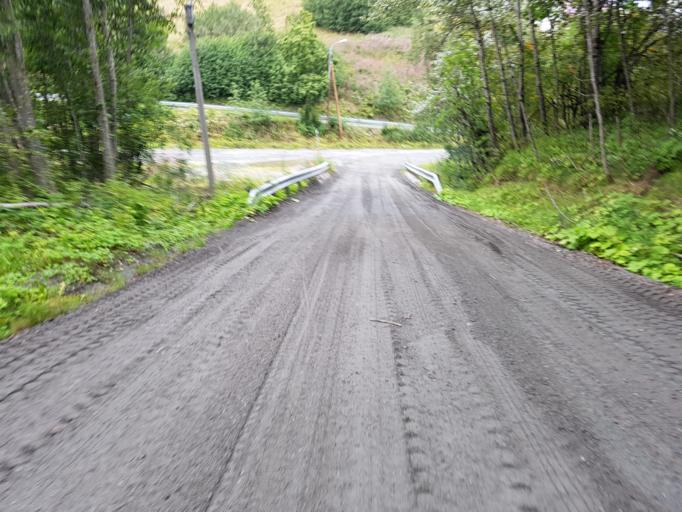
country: NO
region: Sor-Trondelag
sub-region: Trondheim
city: Trondheim
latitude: 63.3844
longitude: 10.3612
